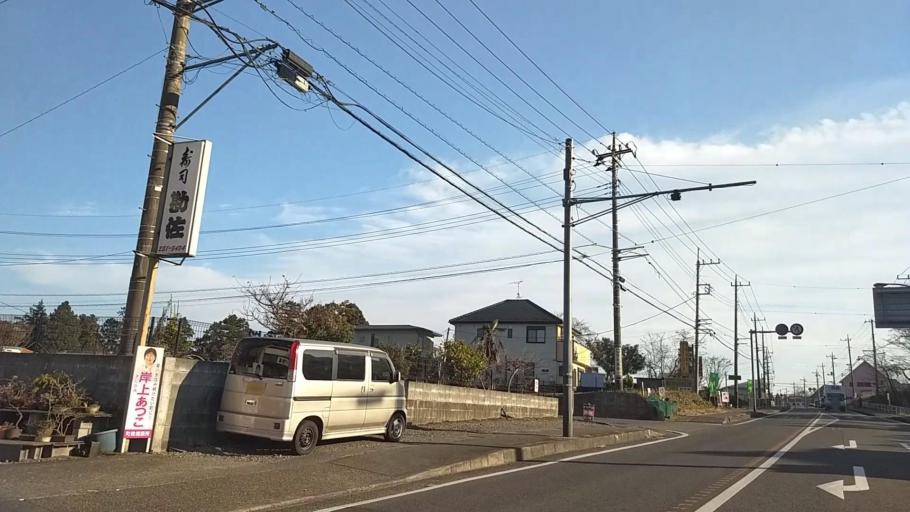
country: JP
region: Kanagawa
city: Zama
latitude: 35.5357
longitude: 139.2720
